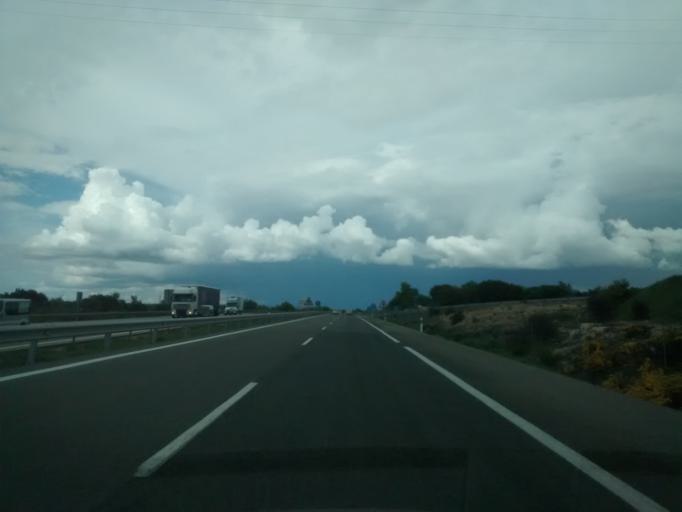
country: ES
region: Castille-La Mancha
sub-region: Provincia de Guadalajara
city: Almadrones
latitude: 40.9017
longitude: -2.7526
